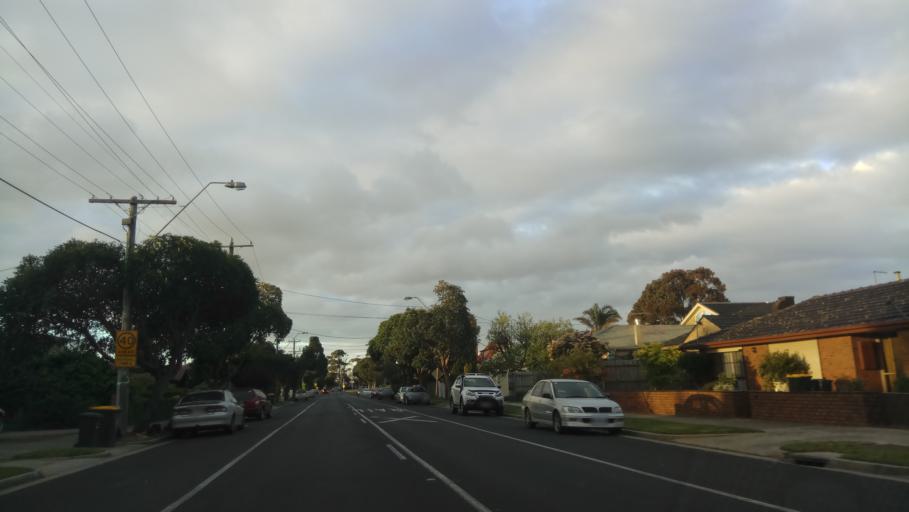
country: AU
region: Victoria
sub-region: Hobsons Bay
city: Seaholme
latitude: -37.8676
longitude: 144.8387
